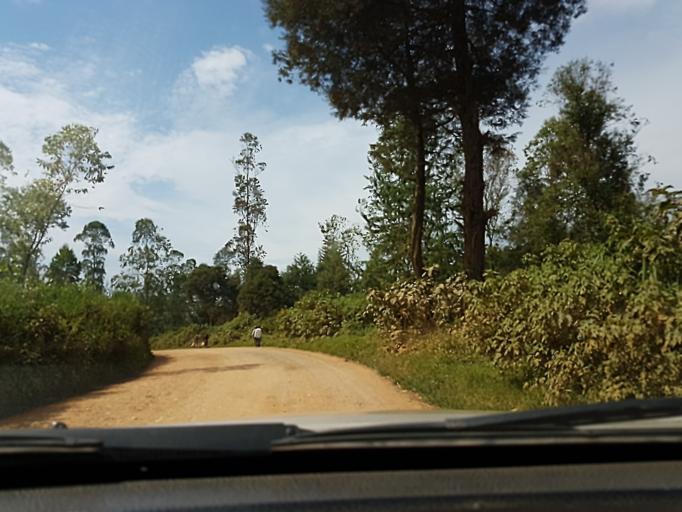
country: CD
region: South Kivu
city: Bukavu
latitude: -2.6369
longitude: 28.8758
